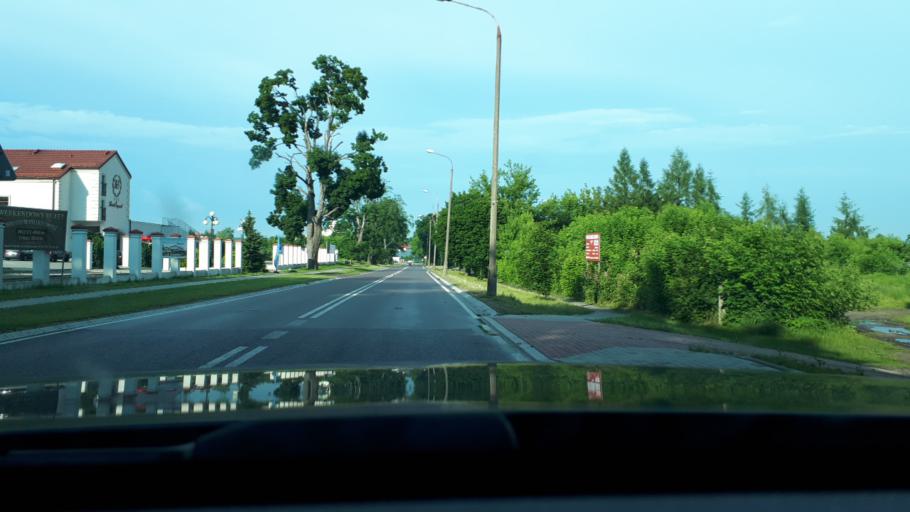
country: PL
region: Podlasie
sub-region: Powiat bialostocki
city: Suprasl
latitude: 53.2087
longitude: 23.3288
